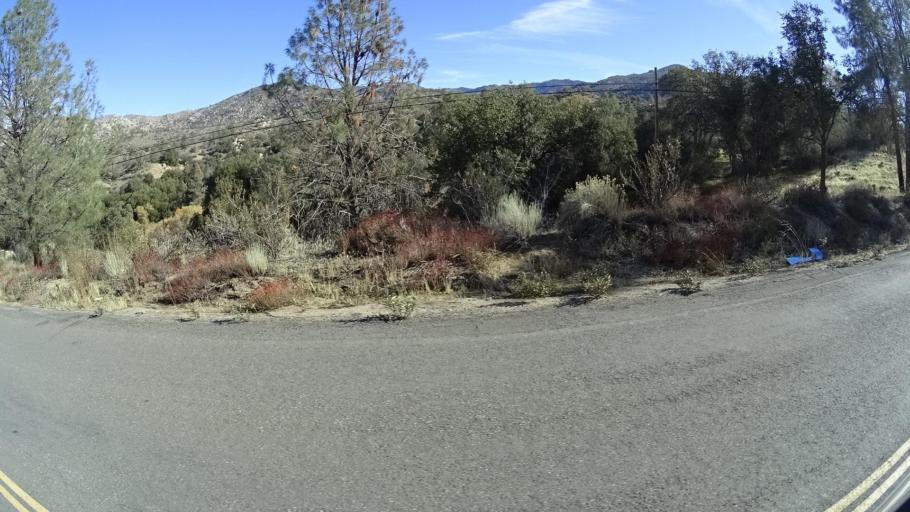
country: US
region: California
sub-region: Kern County
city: Bodfish
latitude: 35.5057
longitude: -118.5213
